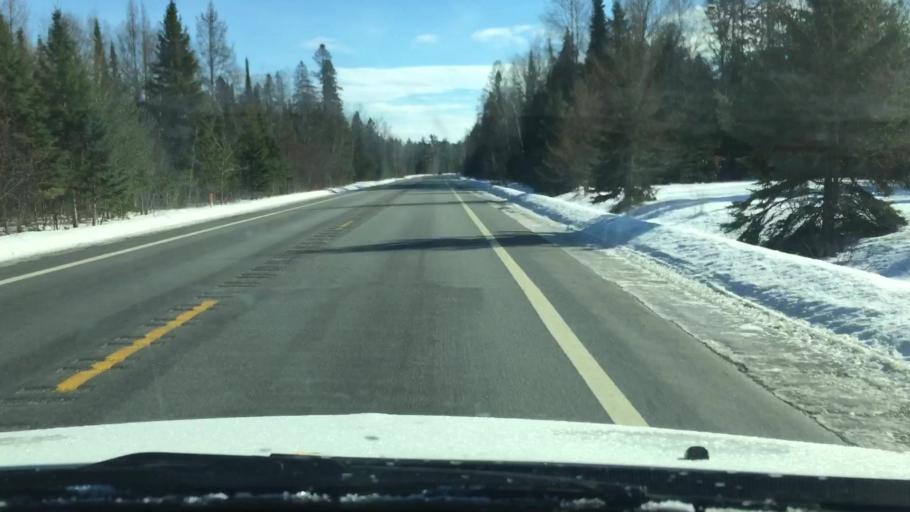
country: US
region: Michigan
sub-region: Charlevoix County
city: East Jordan
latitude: 45.0586
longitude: -85.0762
